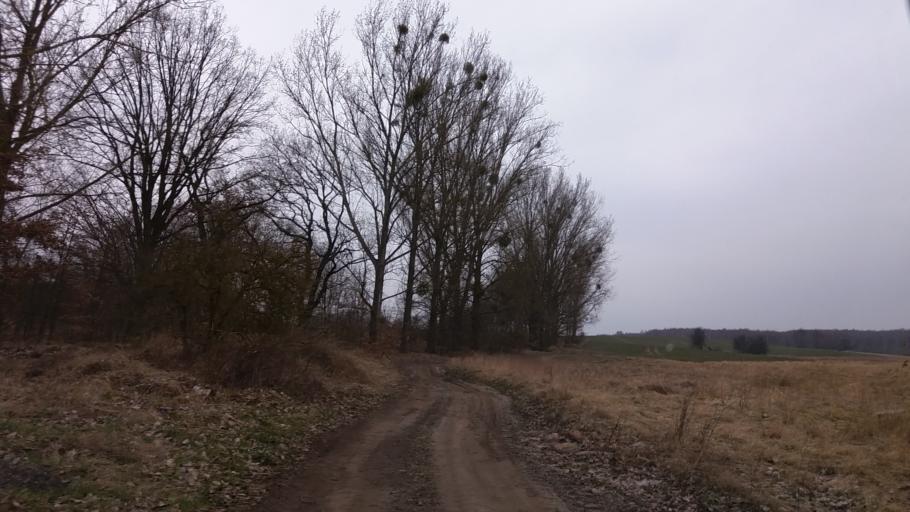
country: PL
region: West Pomeranian Voivodeship
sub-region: Powiat choszczenski
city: Choszczno
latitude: 53.1498
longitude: 15.3507
